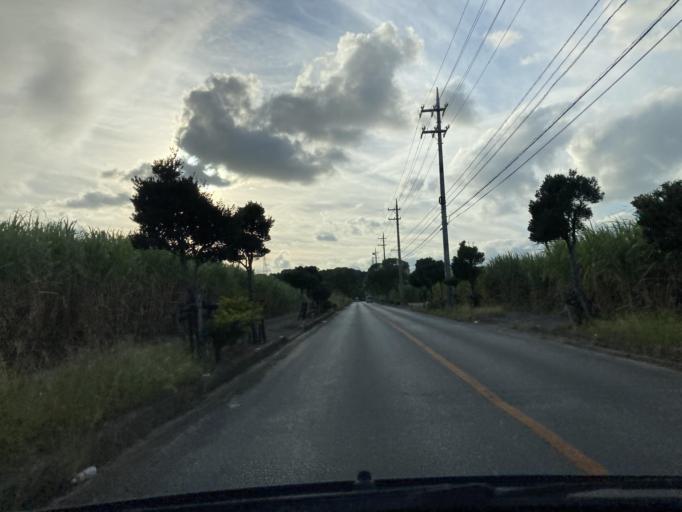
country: JP
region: Okinawa
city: Itoman
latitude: 26.1351
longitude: 127.7038
